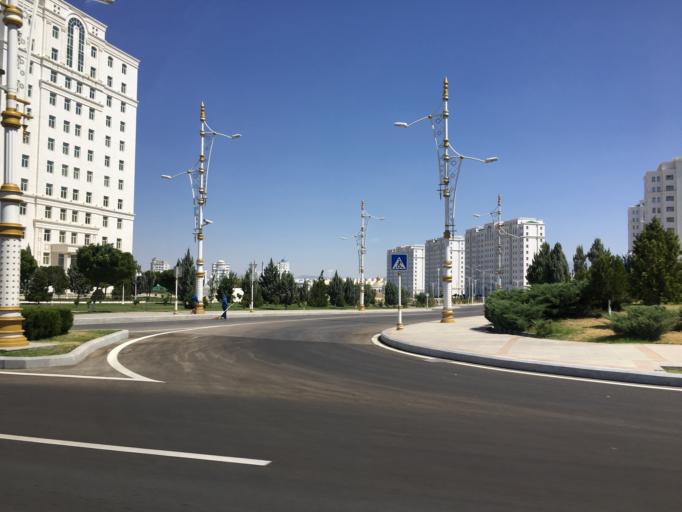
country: TM
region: Ahal
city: Ashgabat
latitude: 37.9234
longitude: 58.3649
